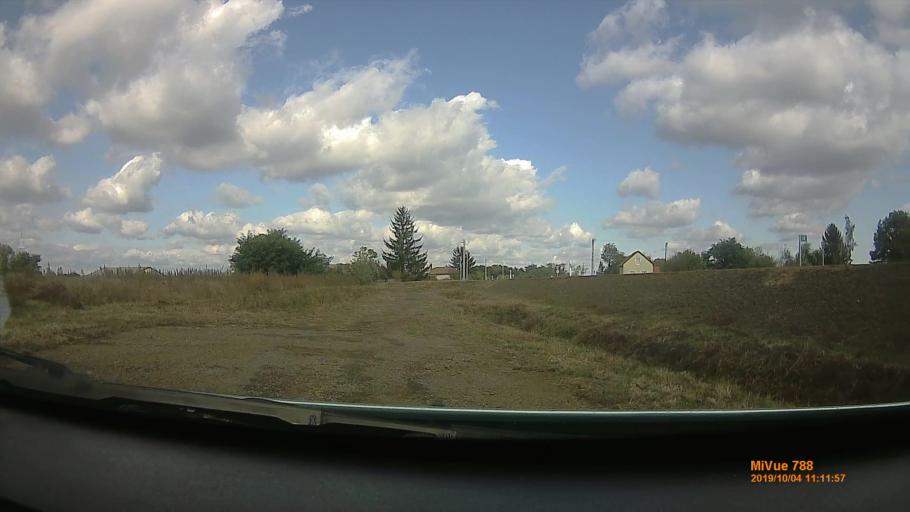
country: HU
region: Szabolcs-Szatmar-Bereg
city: Nyirtelek
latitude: 47.9998
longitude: 21.6729
